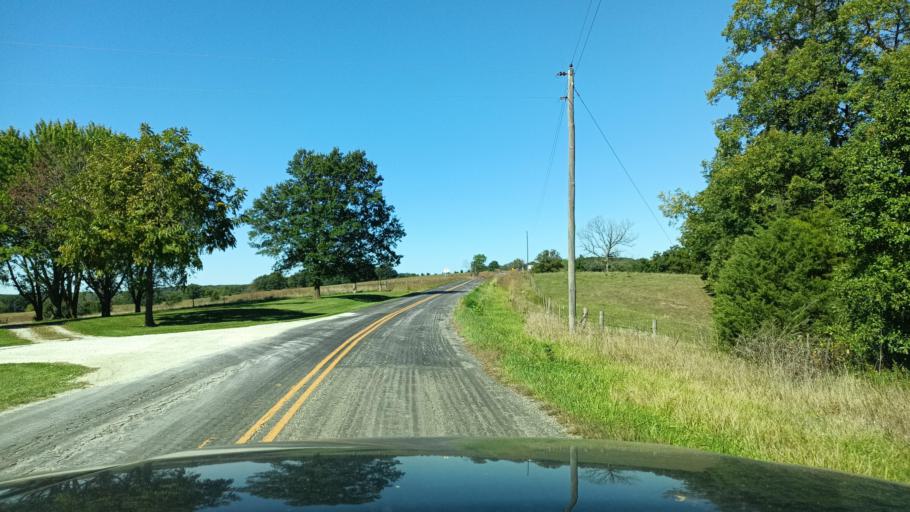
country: US
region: Missouri
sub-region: Scotland County
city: Memphis
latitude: 40.3480
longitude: -92.3313
